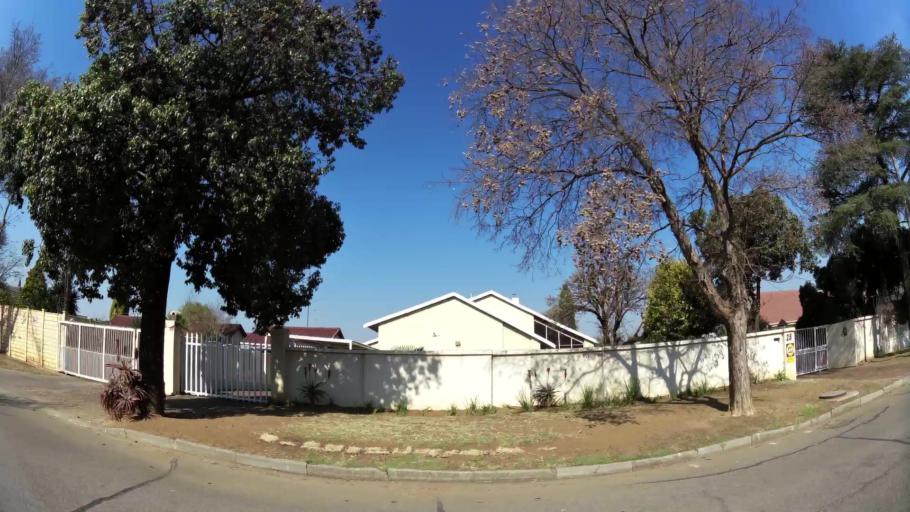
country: ZA
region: Gauteng
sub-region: Ekurhuleni Metropolitan Municipality
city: Boksburg
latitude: -26.2507
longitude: 28.2691
